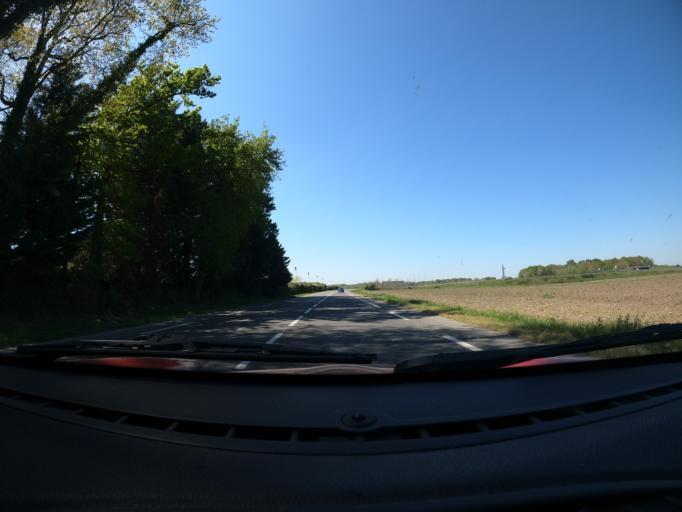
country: FR
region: Aquitaine
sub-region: Departement des Pyrenees-Atlantiques
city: Lescar
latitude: 43.3433
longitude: -0.4143
